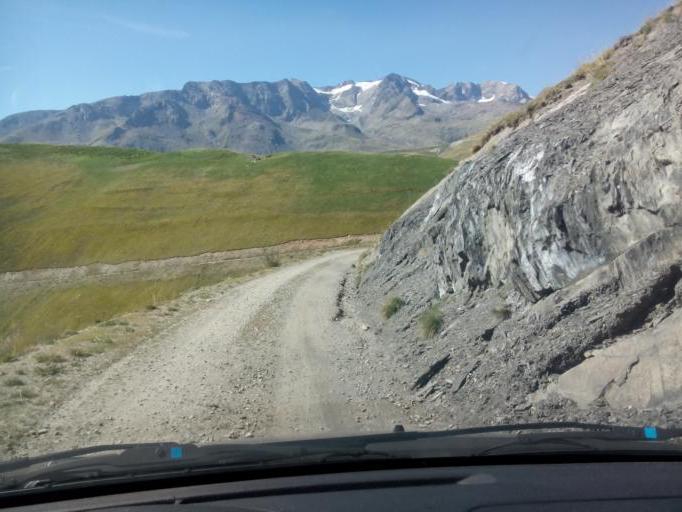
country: FR
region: Rhone-Alpes
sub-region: Departement de l'Isere
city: Mont-de-Lans
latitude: 45.0747
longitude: 6.1954
